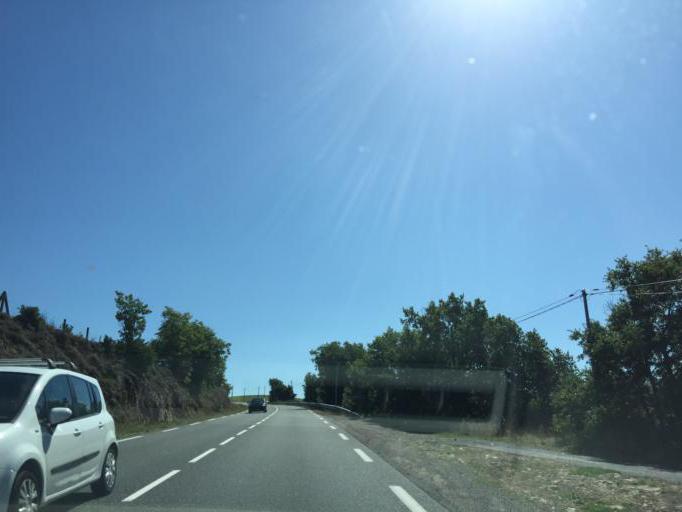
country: FR
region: Midi-Pyrenees
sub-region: Departement de l'Aveyron
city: Saint-Georges-de-Luzencon
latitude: 44.0139
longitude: 2.9907
